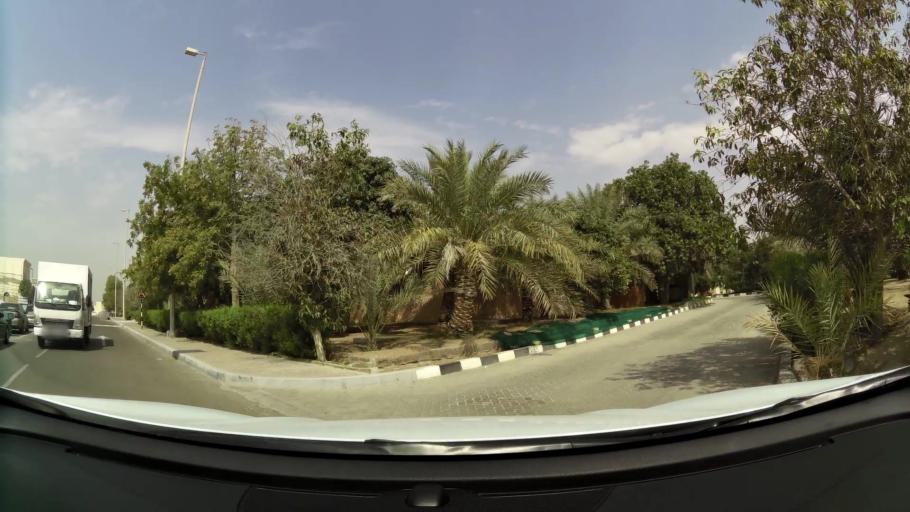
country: AE
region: Abu Dhabi
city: Abu Dhabi
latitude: 24.3104
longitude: 54.6109
